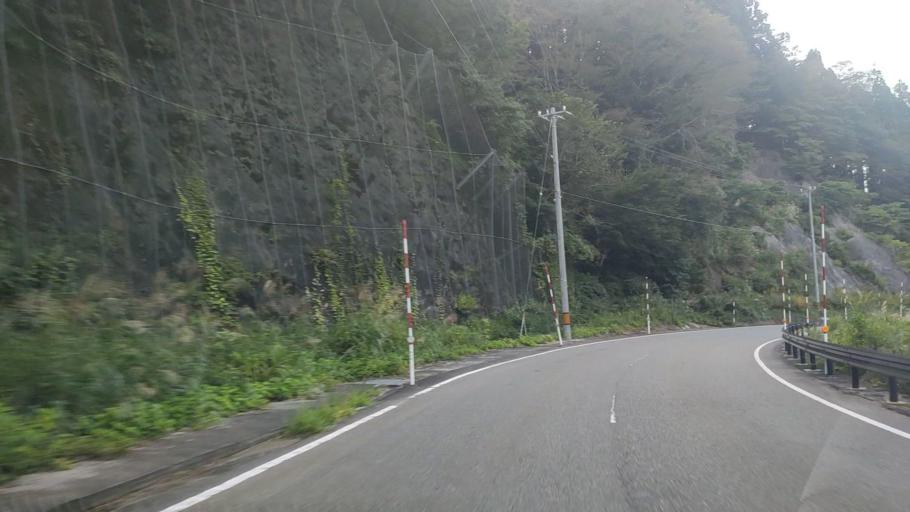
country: JP
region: Toyama
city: Yatsuomachi-higashikumisaka
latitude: 36.4814
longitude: 137.0700
